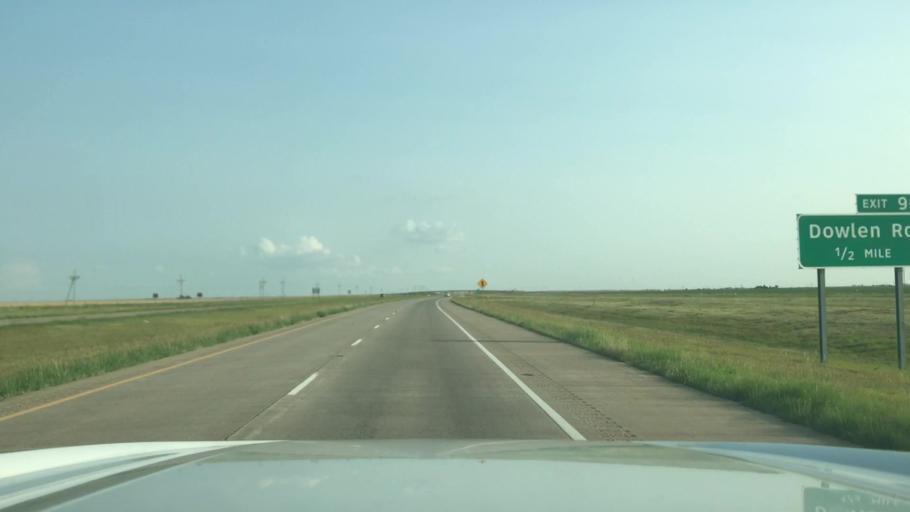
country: US
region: Texas
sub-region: Randall County
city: Canyon
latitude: 34.8520
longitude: -101.8490
